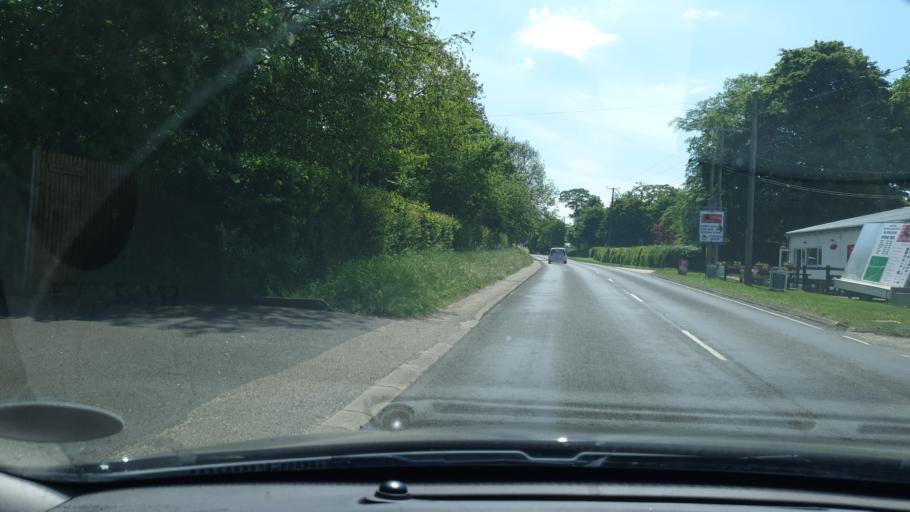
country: GB
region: England
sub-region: Essex
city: Alresford
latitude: 51.8894
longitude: 1.0289
